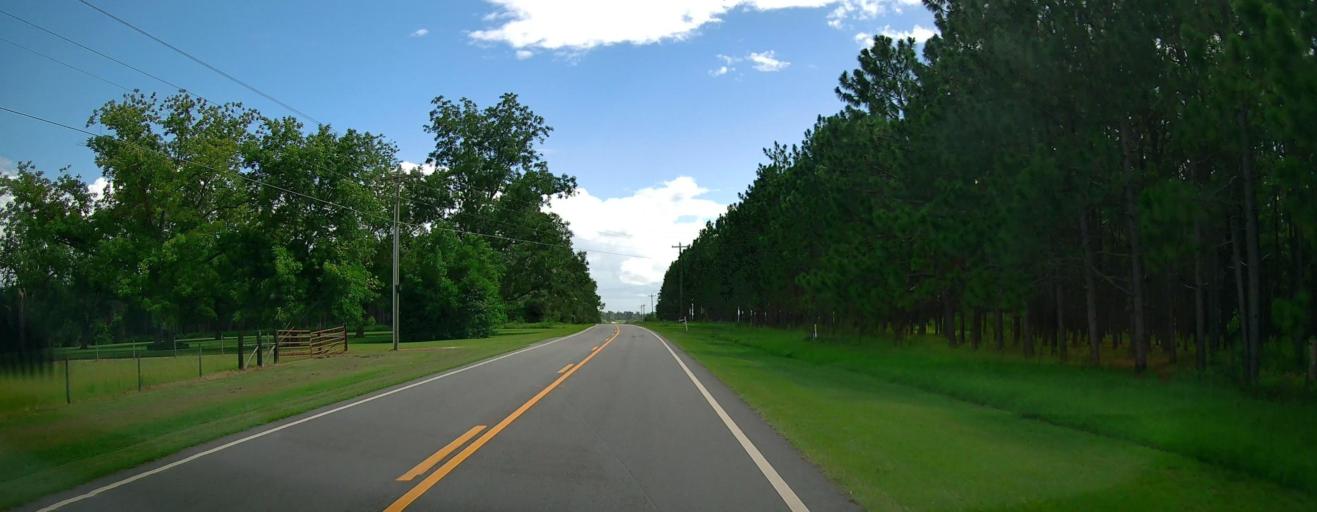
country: US
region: Georgia
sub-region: Irwin County
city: Ocilla
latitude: 31.6205
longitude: -83.1650
